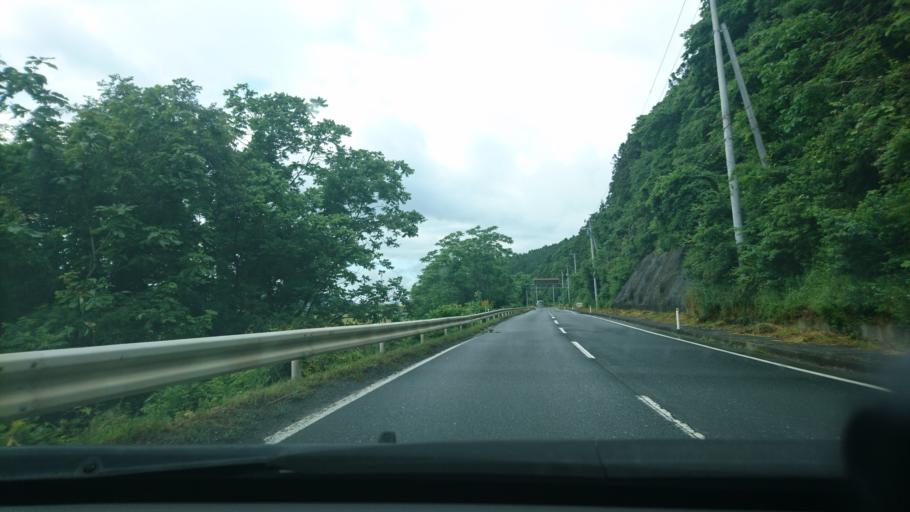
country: JP
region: Miyagi
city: Wakuya
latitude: 38.5963
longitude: 141.3039
